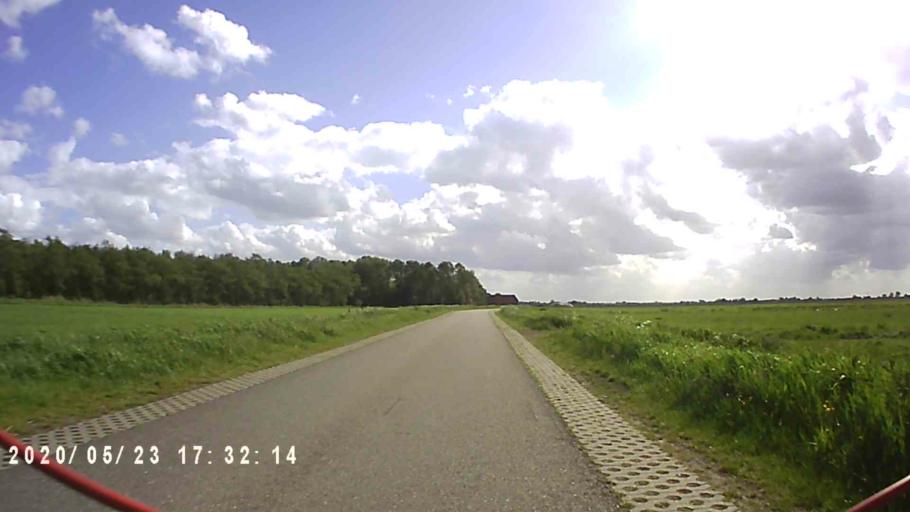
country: NL
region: Groningen
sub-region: Gemeente Slochteren
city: Slochteren
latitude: 53.2550
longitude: 6.7679
